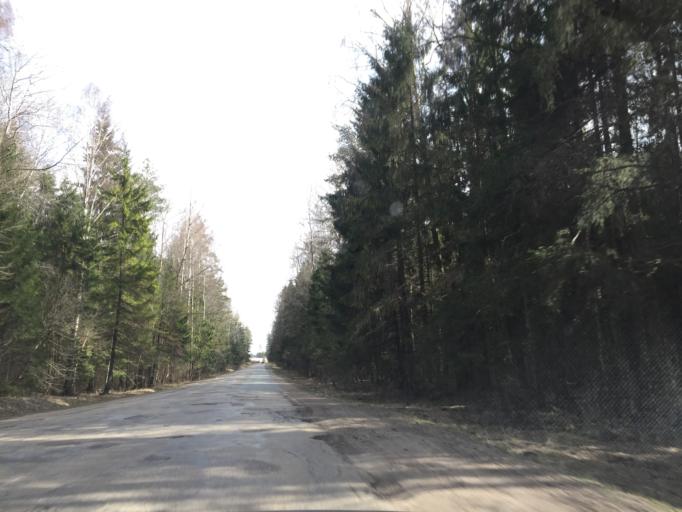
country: LV
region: Ogre
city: Ogre
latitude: 56.8333
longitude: 24.5838
